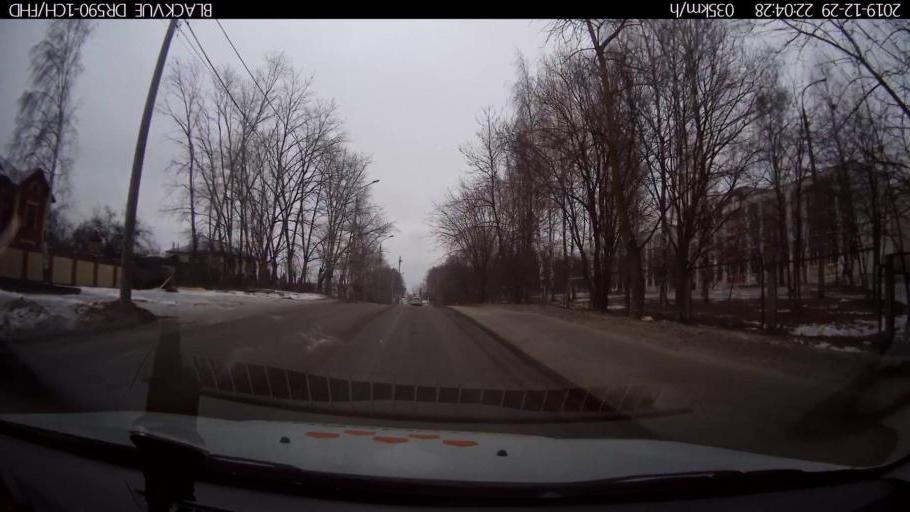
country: RU
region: Nizjnij Novgorod
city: Nizhniy Novgorod
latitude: 56.2273
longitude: 43.9494
